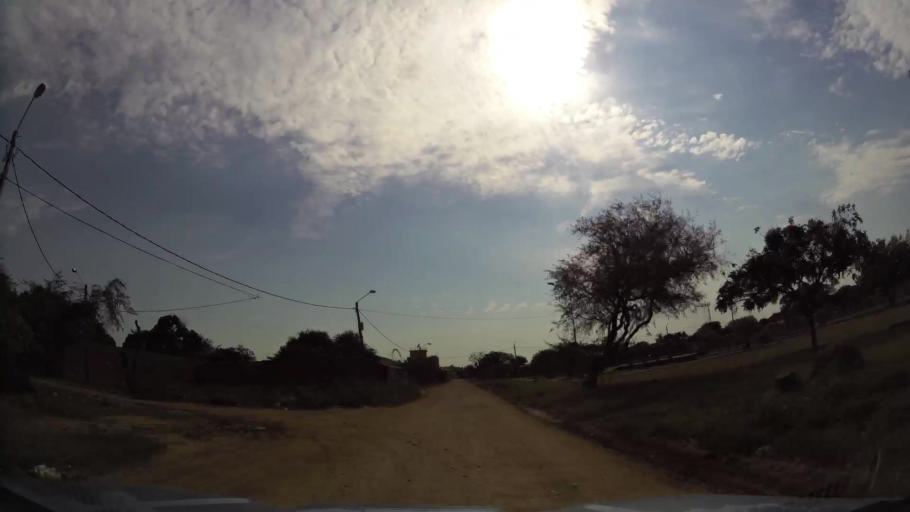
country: BO
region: Santa Cruz
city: Santa Cruz de la Sierra
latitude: -17.7251
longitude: -63.1374
